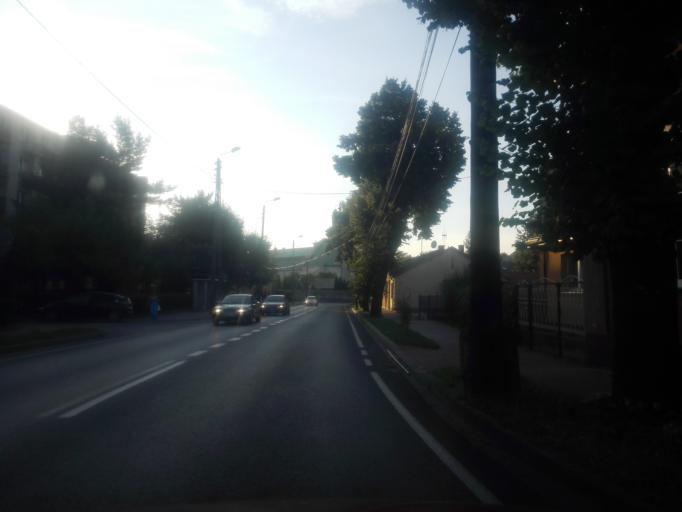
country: PL
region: Lodz Voivodeship
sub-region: Powiat wielunski
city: Wielun
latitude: 51.2163
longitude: 18.5748
